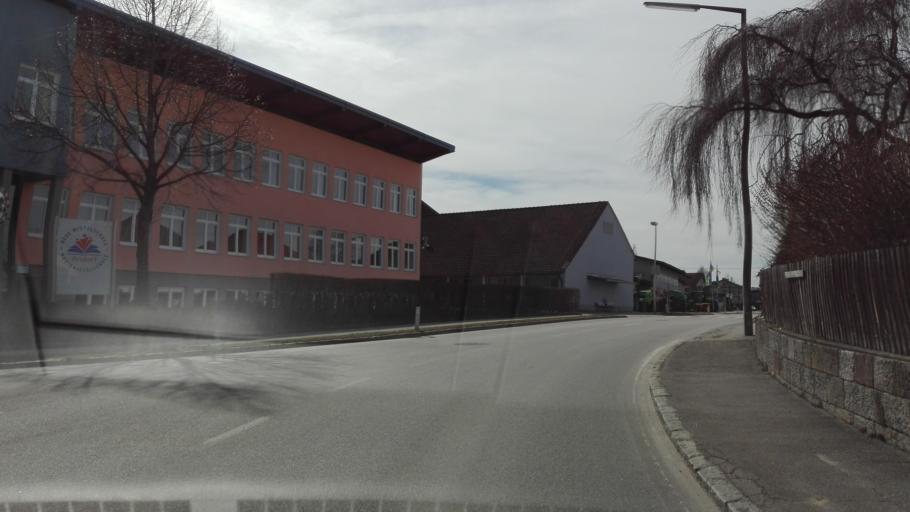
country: AT
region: Upper Austria
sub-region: Politischer Bezirk Scharding
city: Sankt Marienkirchen bei Schaerding
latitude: 48.3724
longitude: 13.5705
